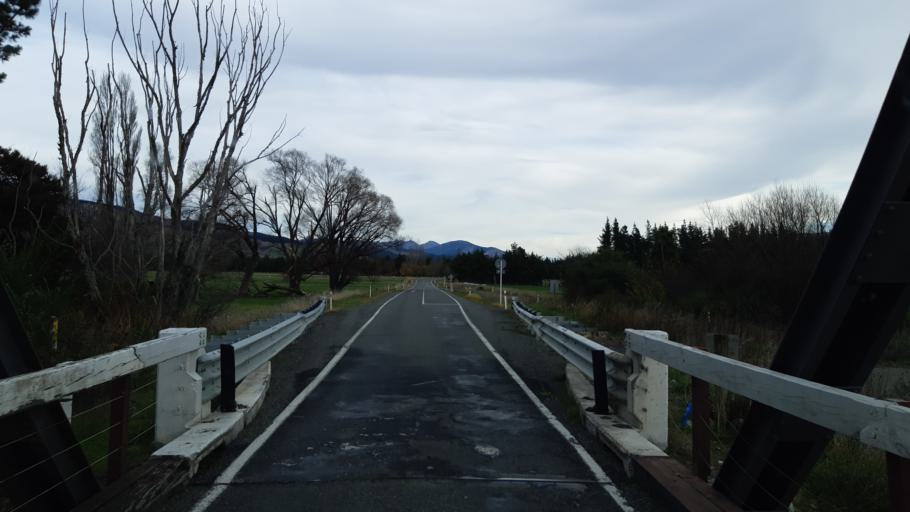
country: NZ
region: Tasman
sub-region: Tasman District
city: Brightwater
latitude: -41.6351
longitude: 173.3241
